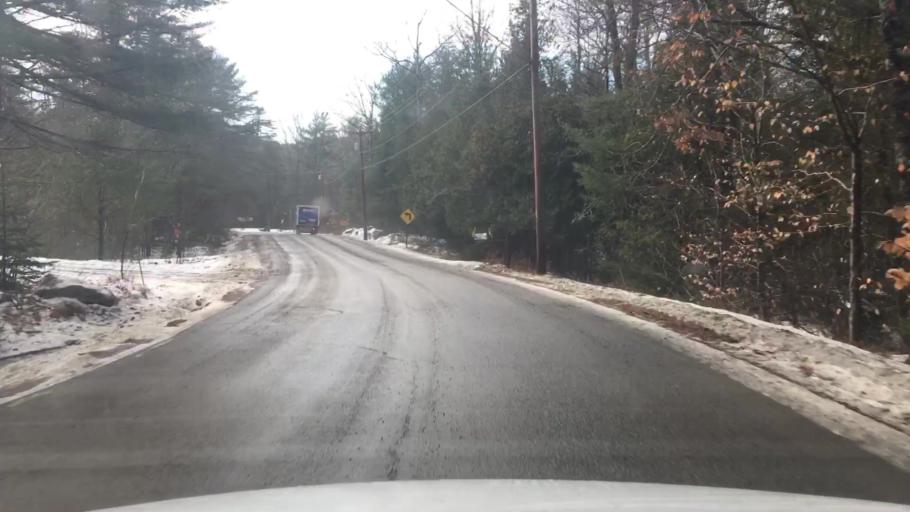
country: US
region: Maine
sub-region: Penobscot County
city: Orrington
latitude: 44.6967
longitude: -68.7564
